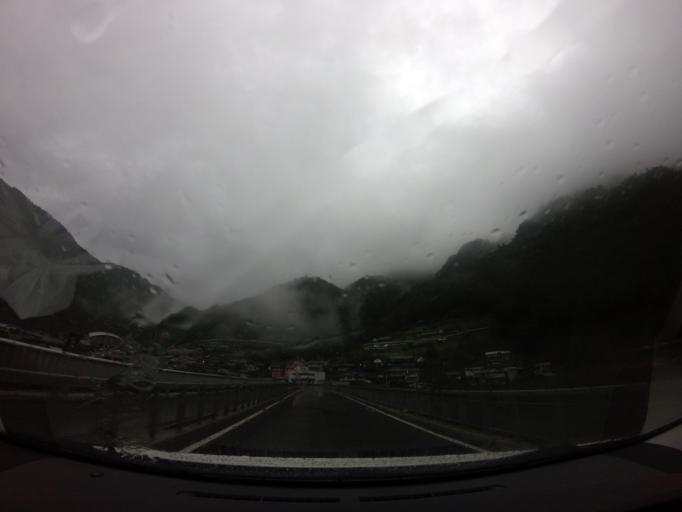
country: JP
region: Wakayama
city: Shingu
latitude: 33.9473
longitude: 135.8046
